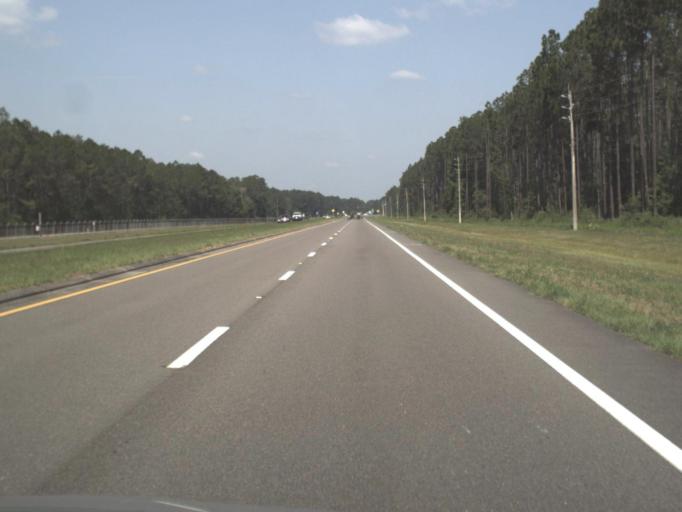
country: US
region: Florida
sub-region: Duval County
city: Baldwin
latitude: 30.2464
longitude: -81.8740
